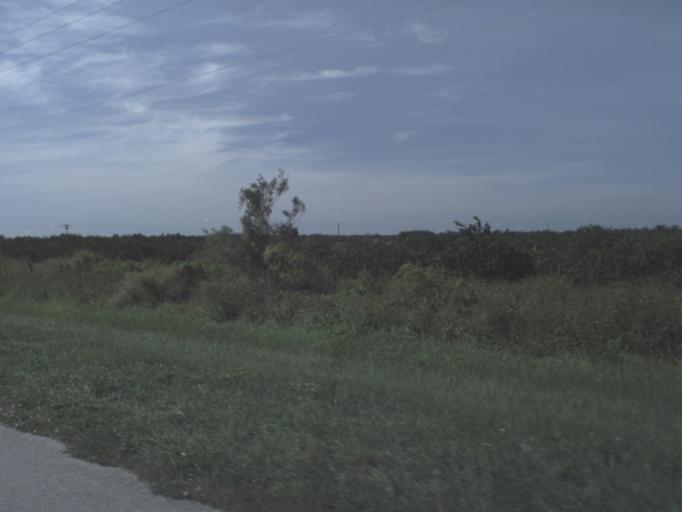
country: US
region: Florida
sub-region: DeSoto County
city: Southeast Arcadia
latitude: 27.1026
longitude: -81.7949
